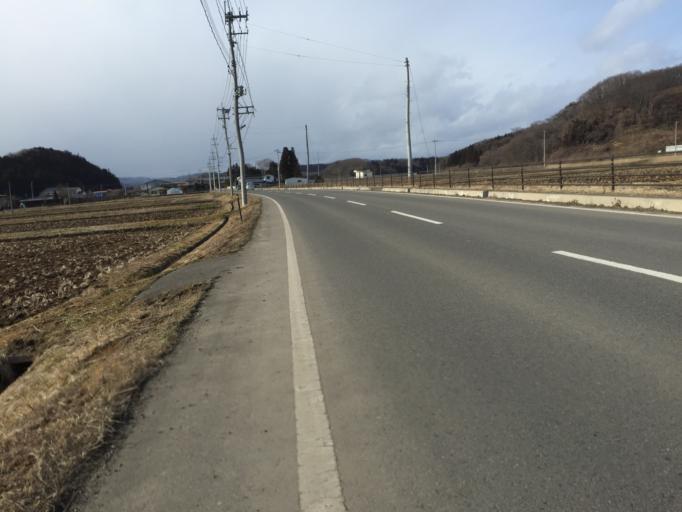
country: JP
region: Tochigi
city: Kuroiso
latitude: 37.1458
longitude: 140.1795
